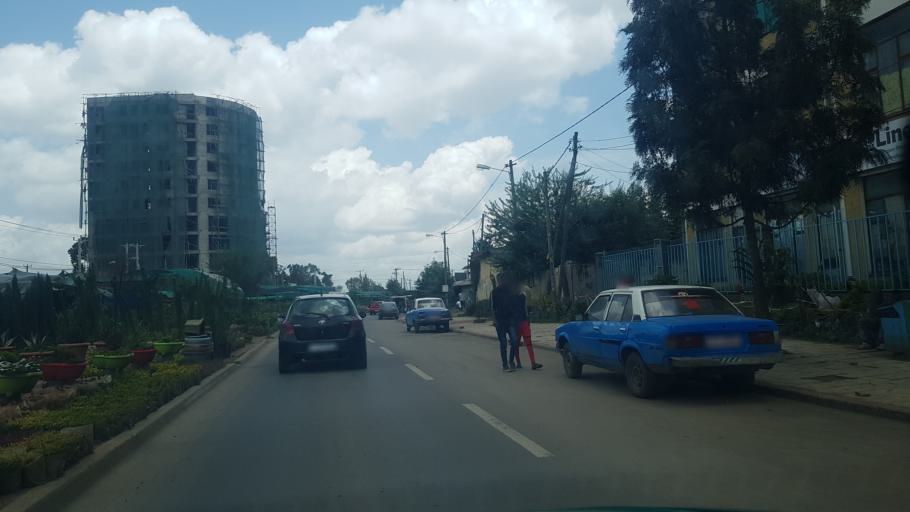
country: ET
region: Adis Abeba
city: Addis Ababa
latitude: 8.9999
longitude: 38.7552
